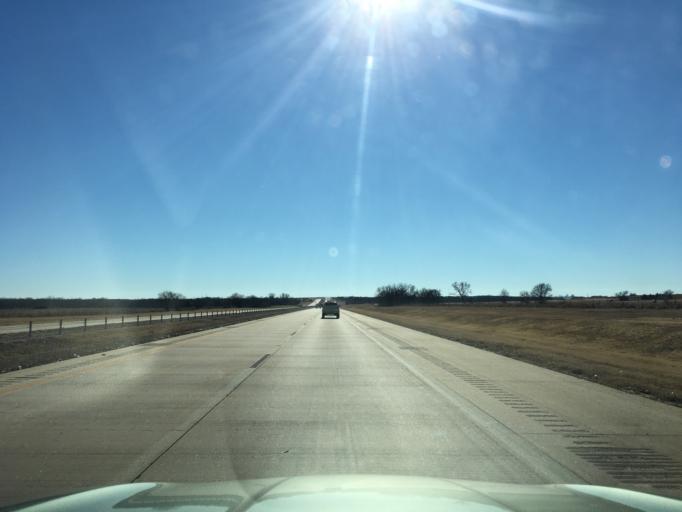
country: US
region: Oklahoma
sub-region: Noble County
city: Perry
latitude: 36.4457
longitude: -97.3271
